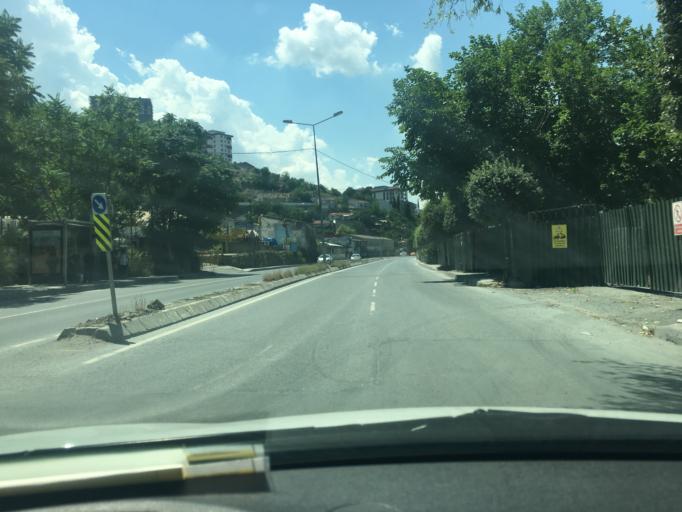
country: TR
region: Istanbul
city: Sisli
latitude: 41.0863
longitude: 28.9428
